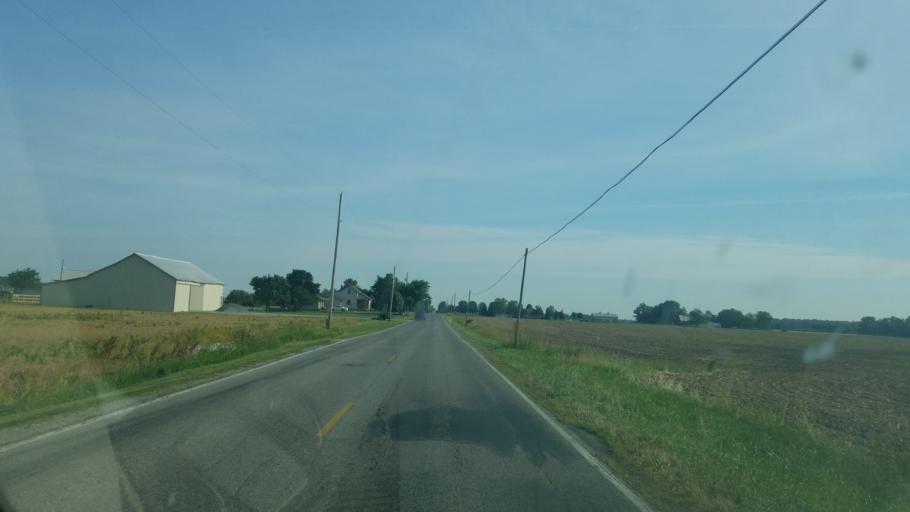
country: US
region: Ohio
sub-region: Hancock County
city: Findlay
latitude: 40.9806
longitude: -83.6985
